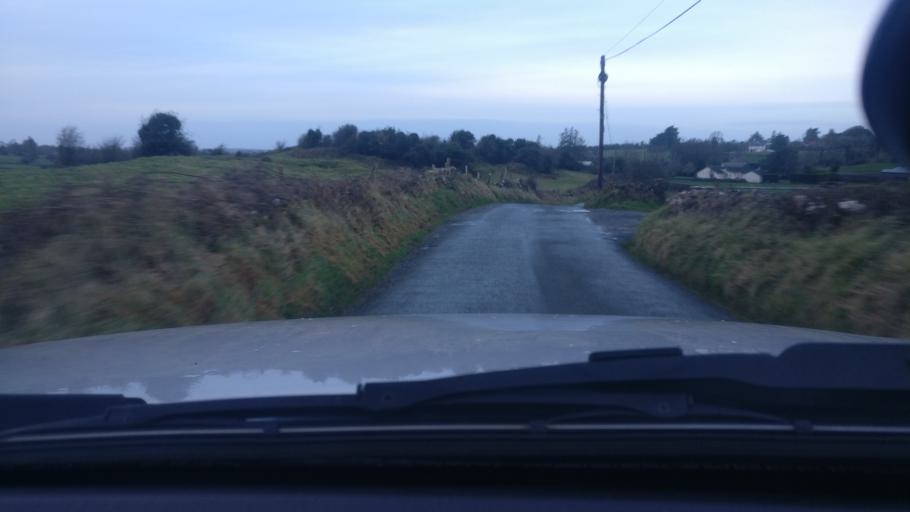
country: IE
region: Connaught
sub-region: County Galway
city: Loughrea
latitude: 53.1677
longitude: -8.5820
